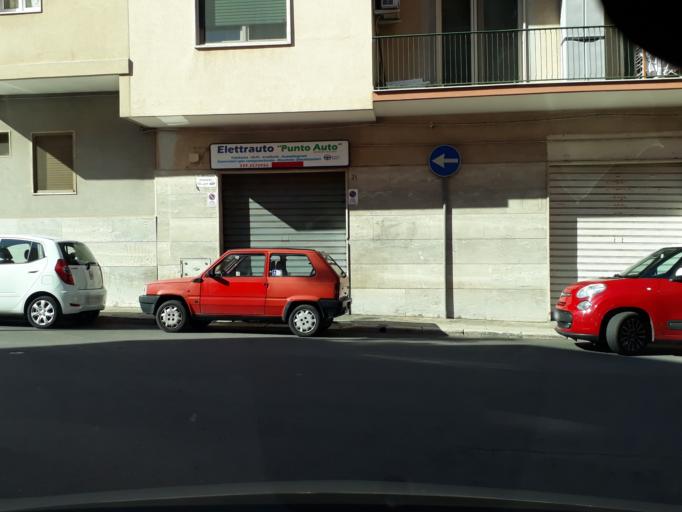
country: IT
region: Apulia
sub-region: Provincia di Bari
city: Monopoli
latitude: 40.9525
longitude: 17.2936
